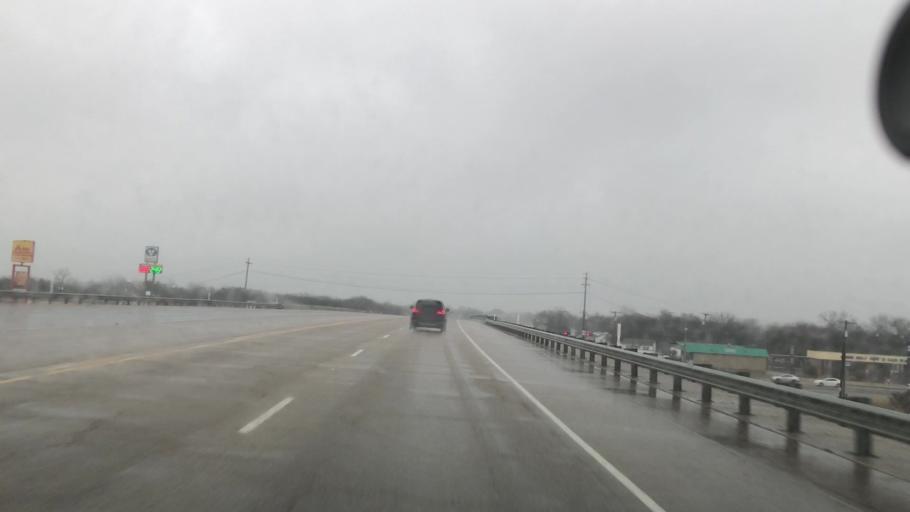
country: US
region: Texas
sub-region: McLennan County
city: Bellmead
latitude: 31.5999
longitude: -97.0906
